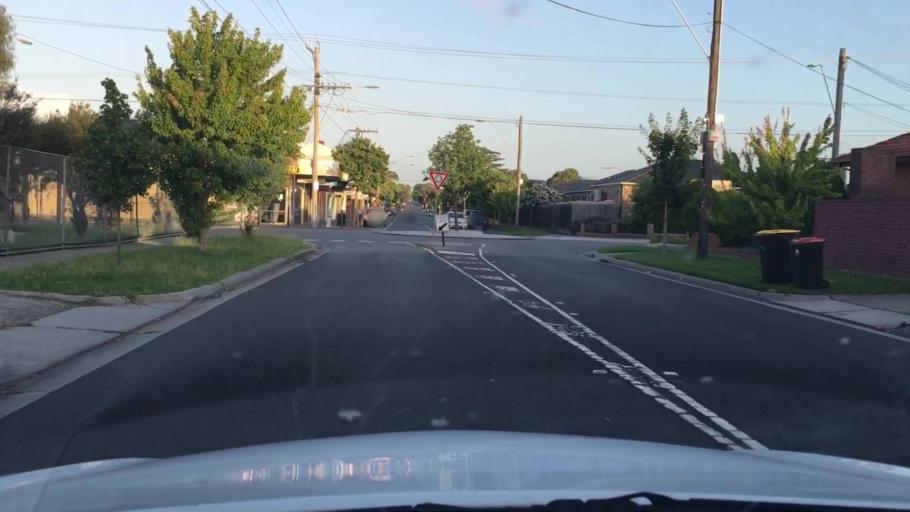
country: AU
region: Victoria
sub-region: Greater Dandenong
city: Dandenong
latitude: -37.9825
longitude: 145.2004
